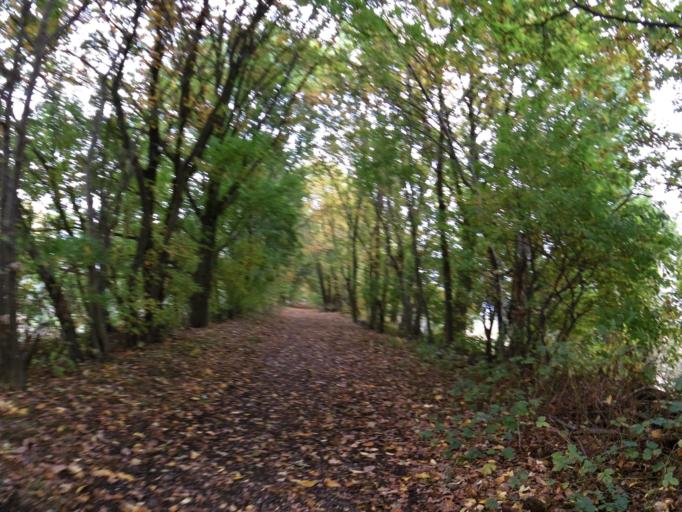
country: NL
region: North Brabant
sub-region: Gemeente Vught
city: Vught
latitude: 51.6844
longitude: 5.2710
